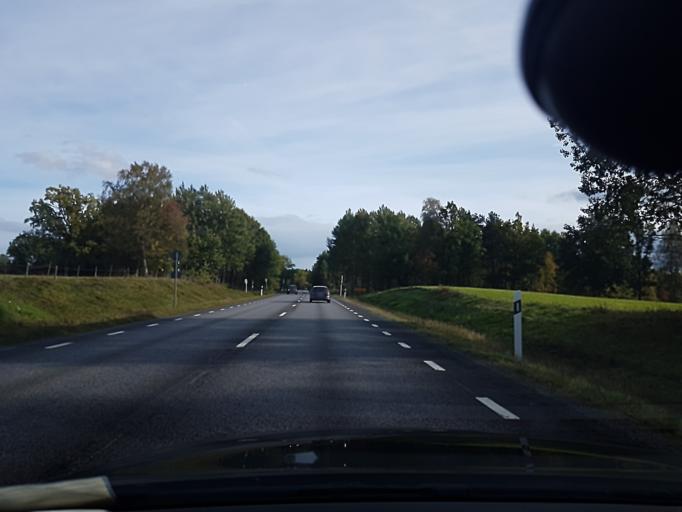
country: SE
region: Joenkoeping
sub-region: Varnamo Kommun
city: Bor
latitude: 57.1440
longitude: 14.1009
